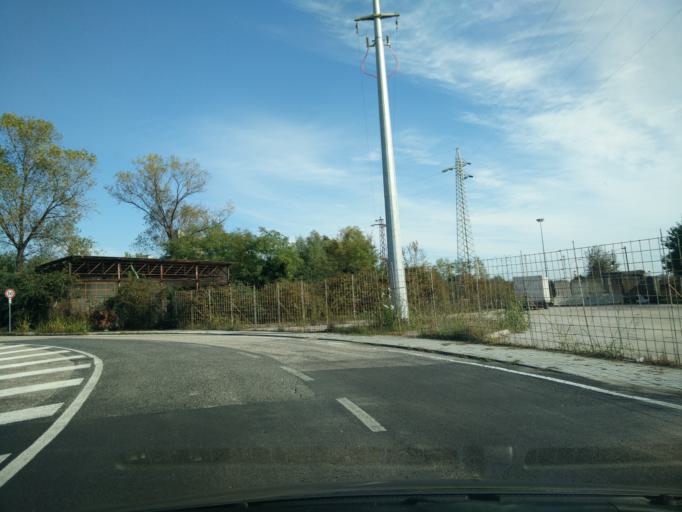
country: IT
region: Veneto
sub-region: Provincia di Venezia
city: Mestre
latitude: 45.4376
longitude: 12.2131
